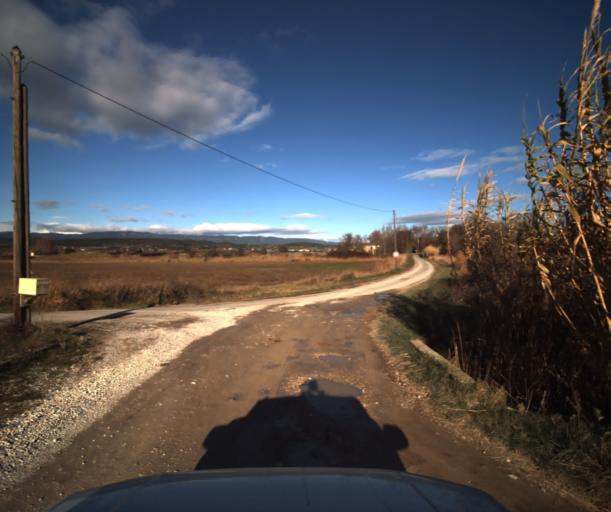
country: FR
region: Provence-Alpes-Cote d'Azur
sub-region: Departement du Vaucluse
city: Pertuis
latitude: 43.6792
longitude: 5.4797
